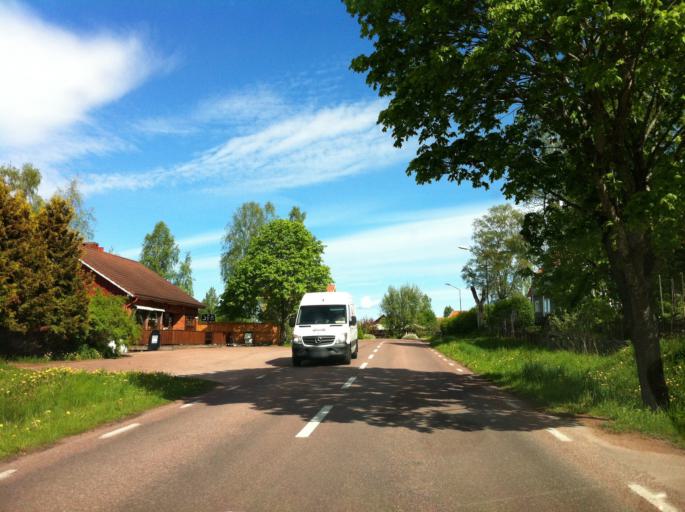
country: SE
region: Dalarna
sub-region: Mora Kommun
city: Mora
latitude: 60.9124
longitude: 14.6163
